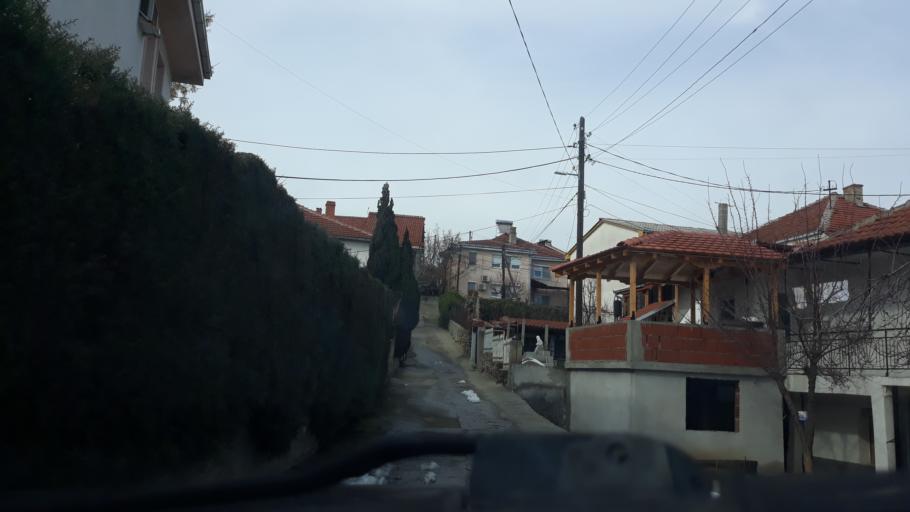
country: MK
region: Negotino
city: Negotino
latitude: 41.4829
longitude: 22.0841
